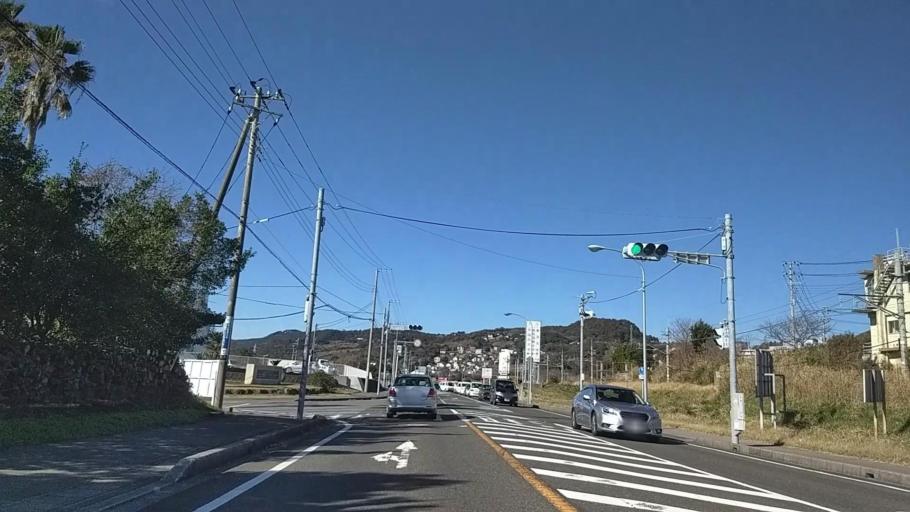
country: JP
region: Chiba
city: Kawaguchi
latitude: 35.0860
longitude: 140.0939
